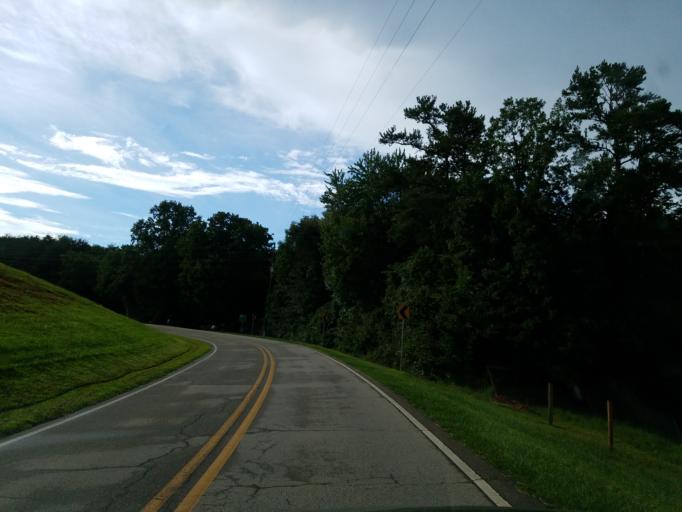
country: US
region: Georgia
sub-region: White County
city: Cleveland
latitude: 34.6147
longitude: -83.8688
